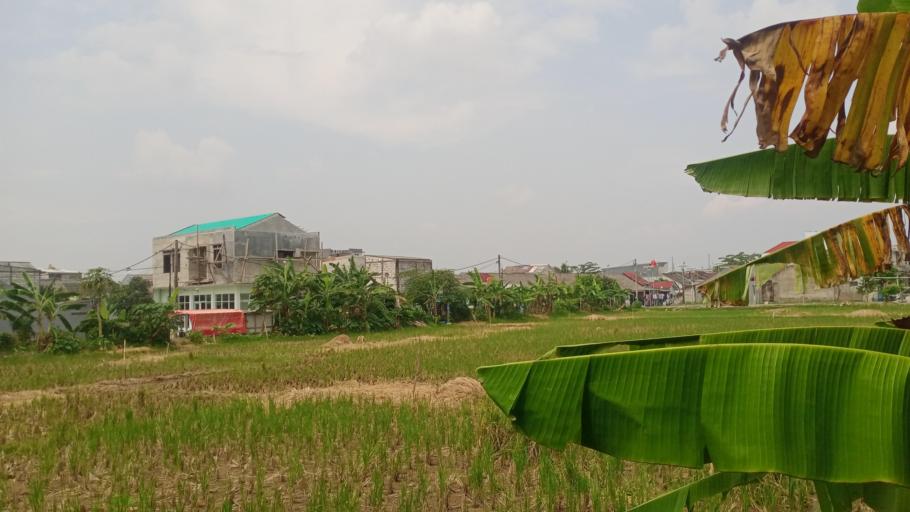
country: ID
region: West Java
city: Cikarang
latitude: -6.3523
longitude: 107.1072
